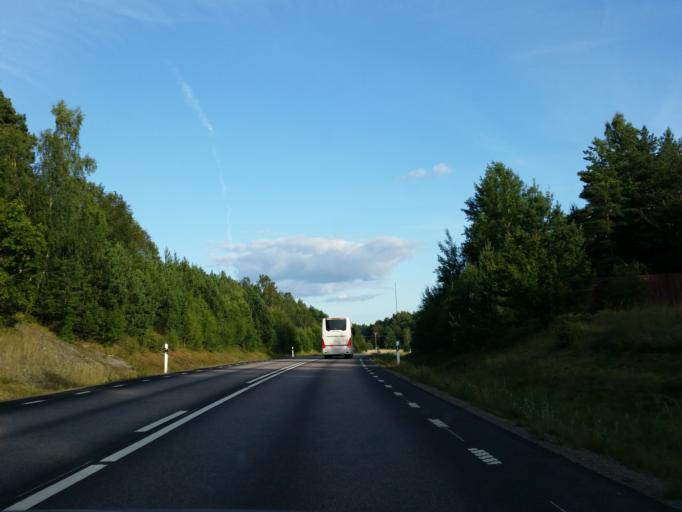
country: SE
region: Soedermanland
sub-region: Gnesta Kommun
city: Gnesta
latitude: 59.0464
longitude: 17.2868
